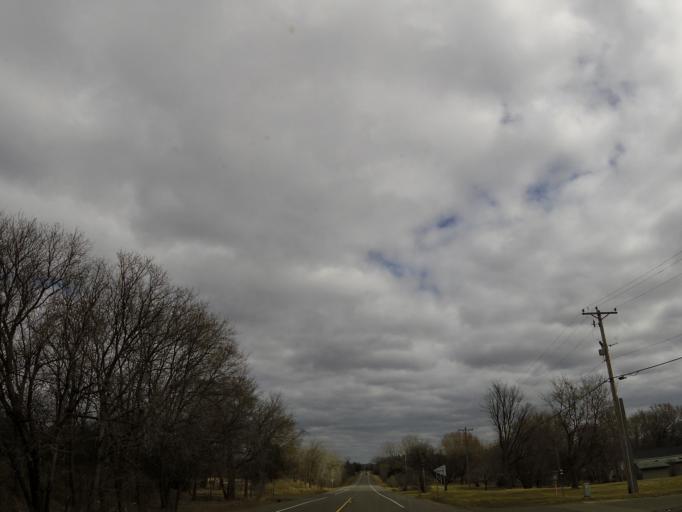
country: US
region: Minnesota
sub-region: Washington County
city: Lake Elmo
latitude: 44.9635
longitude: -92.8758
